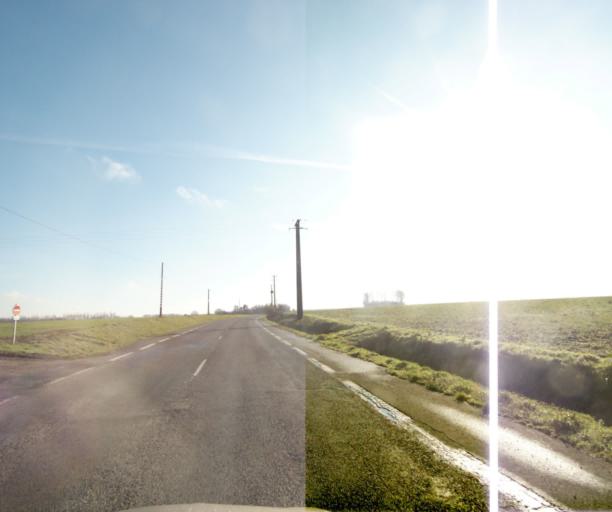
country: FR
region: Nord-Pas-de-Calais
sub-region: Departement du Nord
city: Saultain
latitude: 50.3265
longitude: 3.5613
